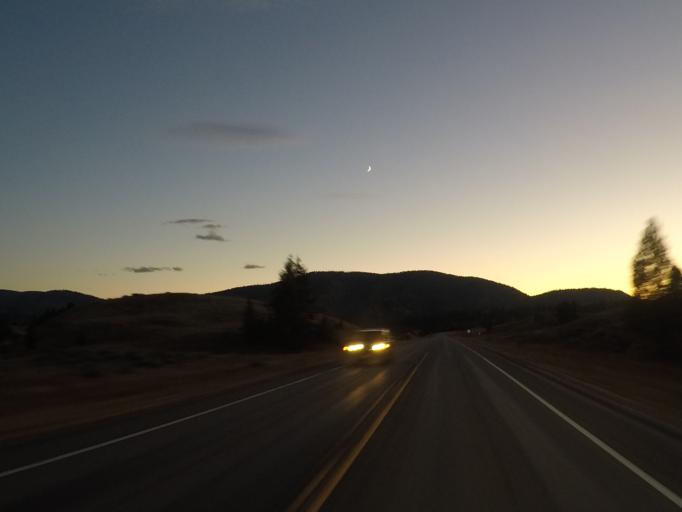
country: US
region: Montana
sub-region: Missoula County
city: Seeley Lake
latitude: 47.0354
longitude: -113.2307
